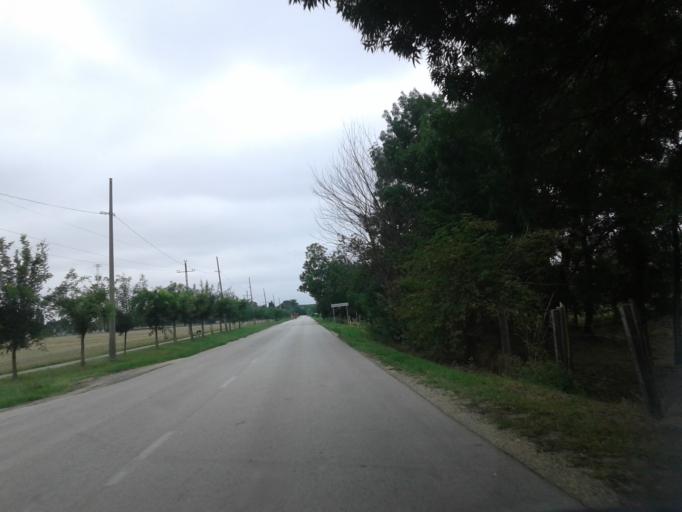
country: HU
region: Bacs-Kiskun
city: Harta
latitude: 46.6929
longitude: 19.0197
